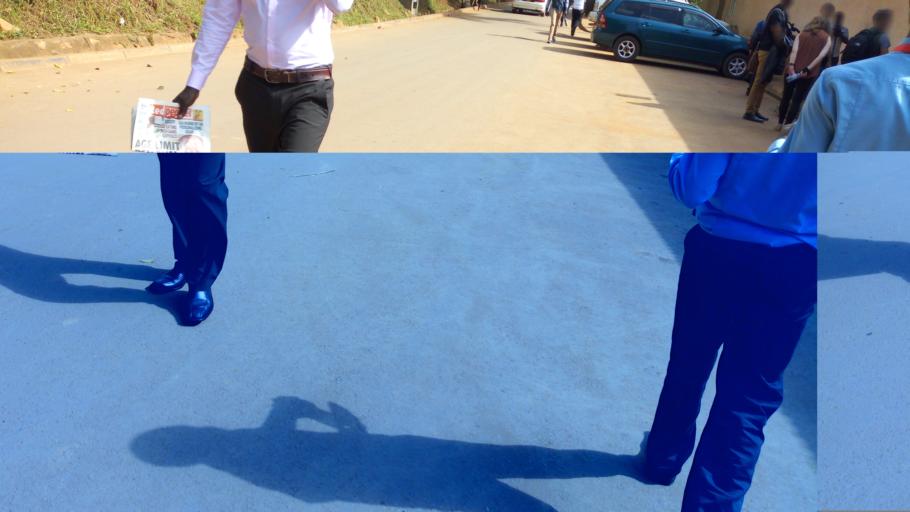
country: UG
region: Central Region
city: Kampala Central Division
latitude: 0.3349
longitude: 32.5690
